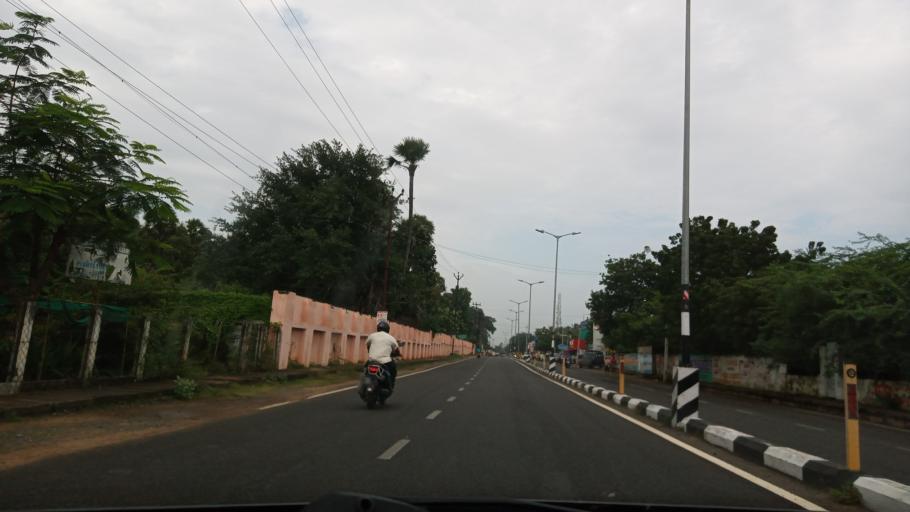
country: IN
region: Tamil Nadu
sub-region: Villupuram
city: Auroville
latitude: 12.0133
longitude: 79.8577
